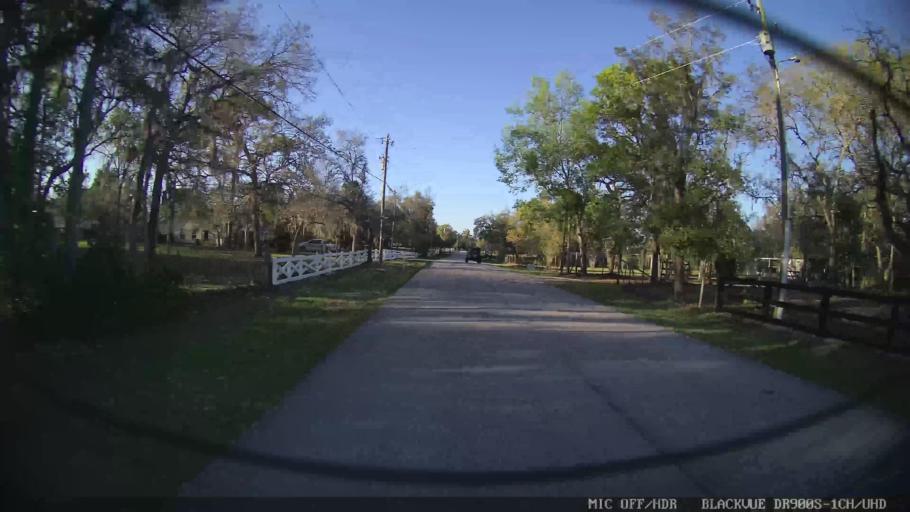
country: US
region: Florida
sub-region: Pasco County
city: Shady Hills
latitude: 28.4105
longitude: -82.5738
